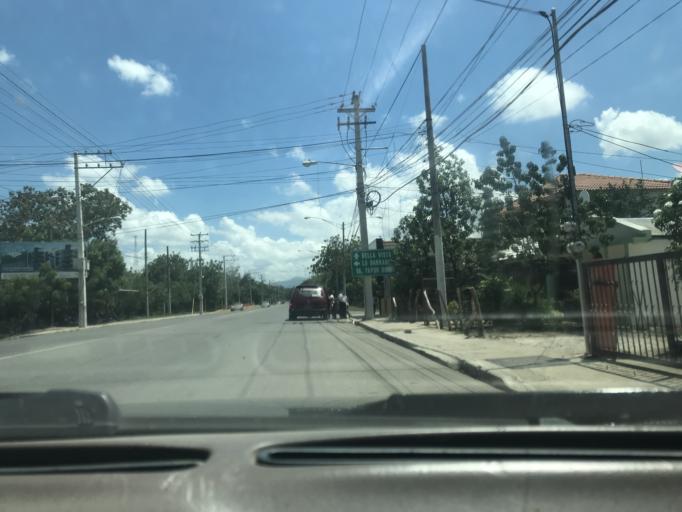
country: DO
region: Santiago
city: Santiago de los Caballeros
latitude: 19.4129
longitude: -70.7178
